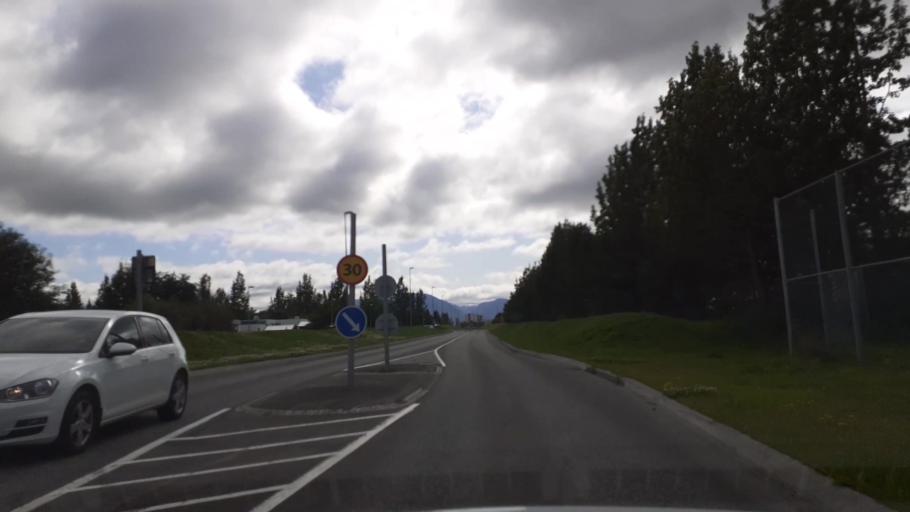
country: IS
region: Northeast
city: Akureyri
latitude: 65.6759
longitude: -18.1105
